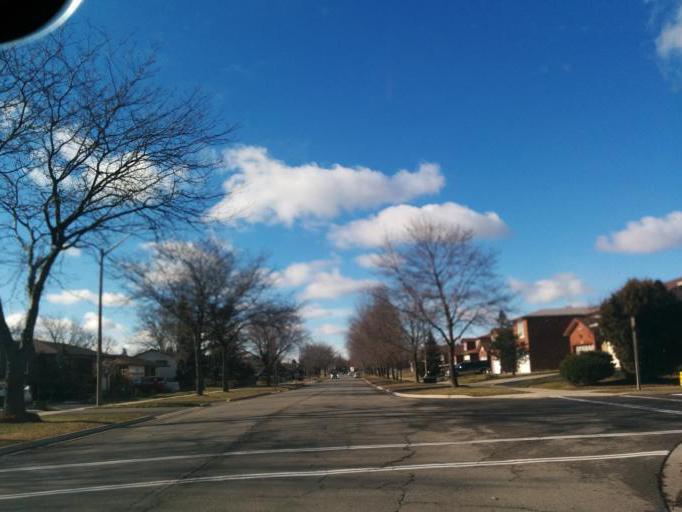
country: CA
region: Ontario
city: Mississauga
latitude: 43.5720
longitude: -79.6174
